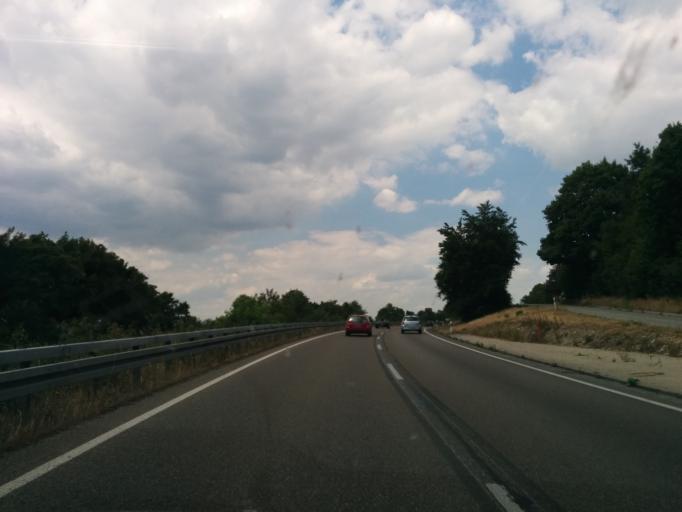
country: DE
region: Bavaria
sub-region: Swabia
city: Donauwoerth
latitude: 48.7196
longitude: 10.7872
